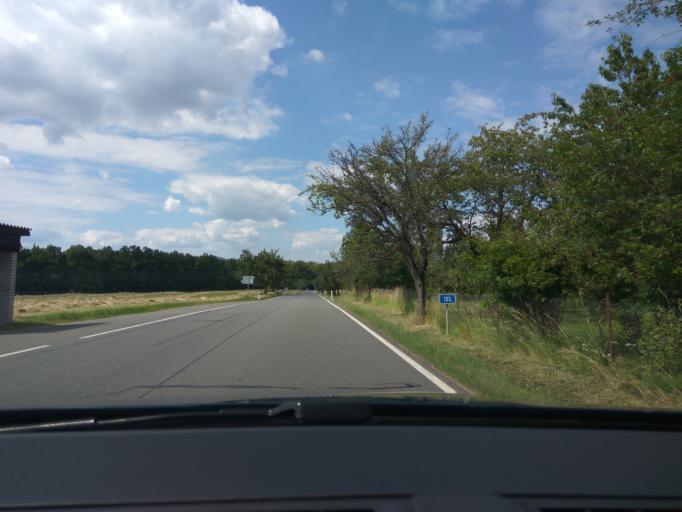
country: CZ
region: Jihocesky
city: Milevsko
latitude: 49.4133
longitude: 14.3586
